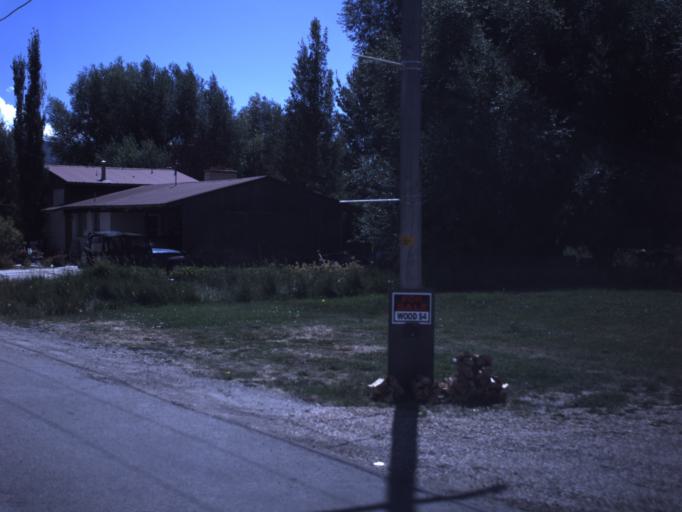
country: US
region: Utah
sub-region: Summit County
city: Oakley
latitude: 40.7120
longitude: -111.2988
